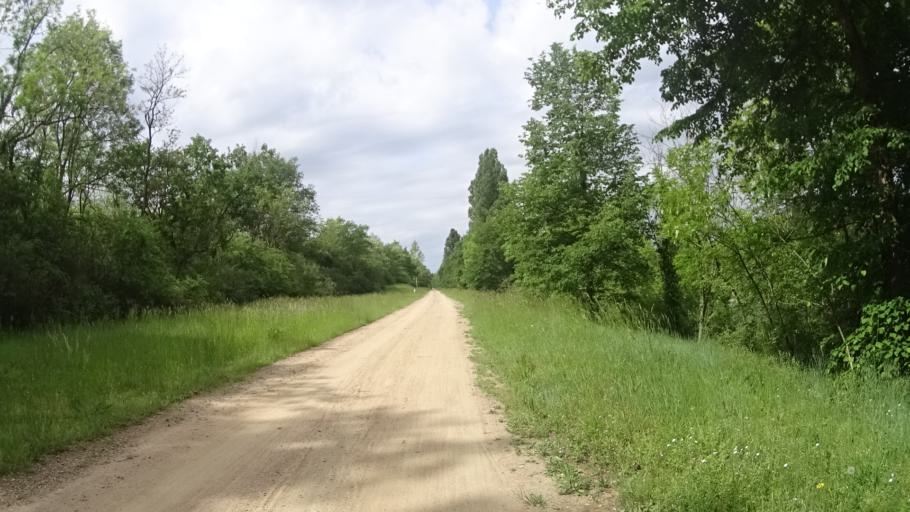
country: FR
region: Alsace
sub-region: Departement du Haut-Rhin
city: Kembs
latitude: 47.7070
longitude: 7.5237
